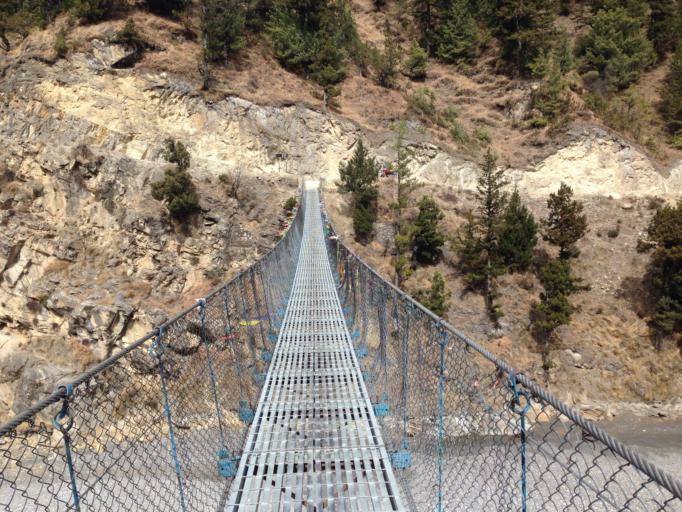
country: NP
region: Western Region
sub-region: Dhawalagiri Zone
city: Jomsom
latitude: 28.6718
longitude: 83.5975
